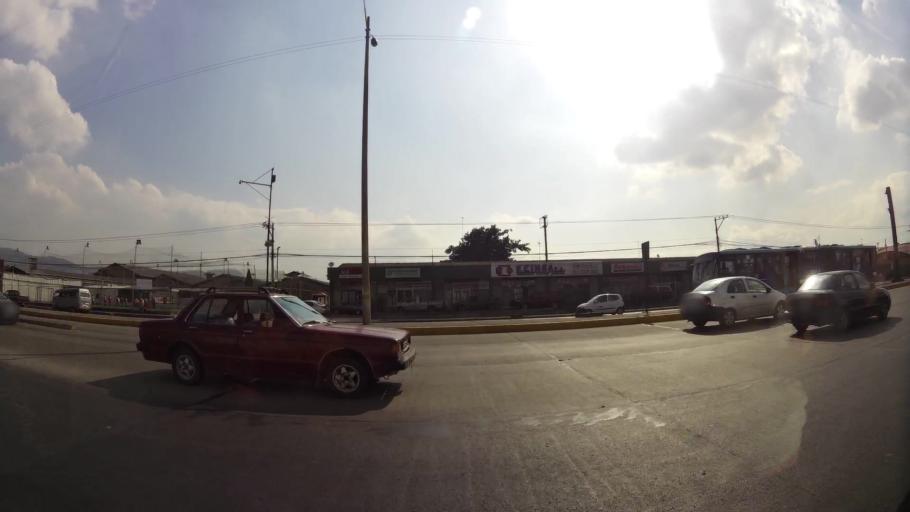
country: EC
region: Guayas
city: Guayaquil
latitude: -2.1332
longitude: -79.9333
